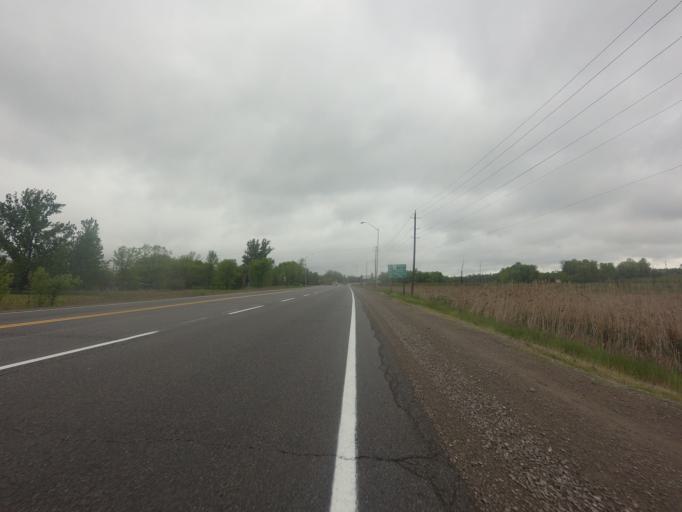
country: CA
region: Ontario
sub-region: Lanark County
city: Smiths Falls
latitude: 44.8219
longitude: -76.0908
